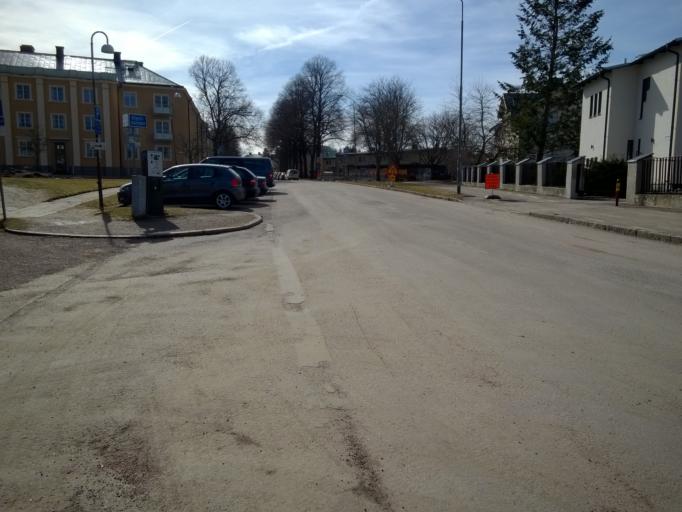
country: SE
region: Gaevleborg
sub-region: Gavle Kommun
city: Gavle
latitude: 60.6710
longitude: 17.1404
